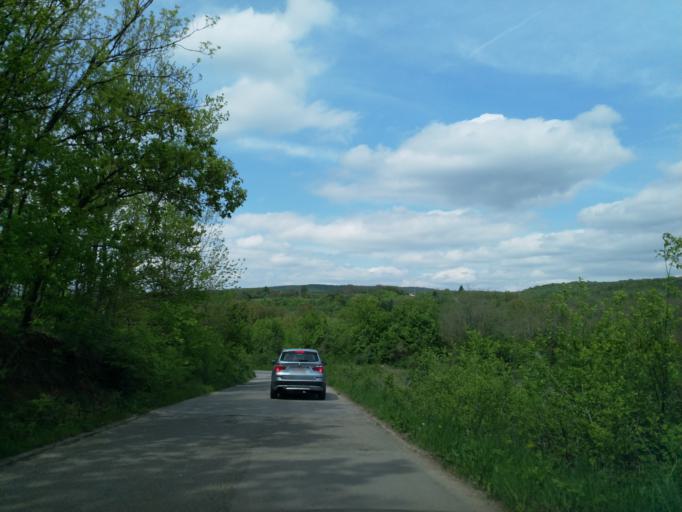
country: RS
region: Central Serbia
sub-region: Pomoravski Okrug
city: Cuprija
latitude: 43.9517
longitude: 21.4865
